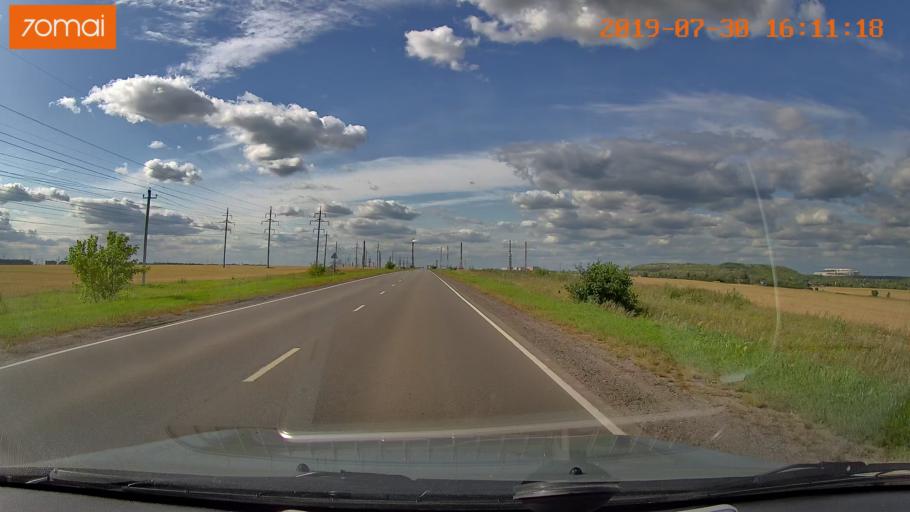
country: RU
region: Moskovskaya
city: Lopatinskiy
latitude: 55.2738
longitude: 38.7123
